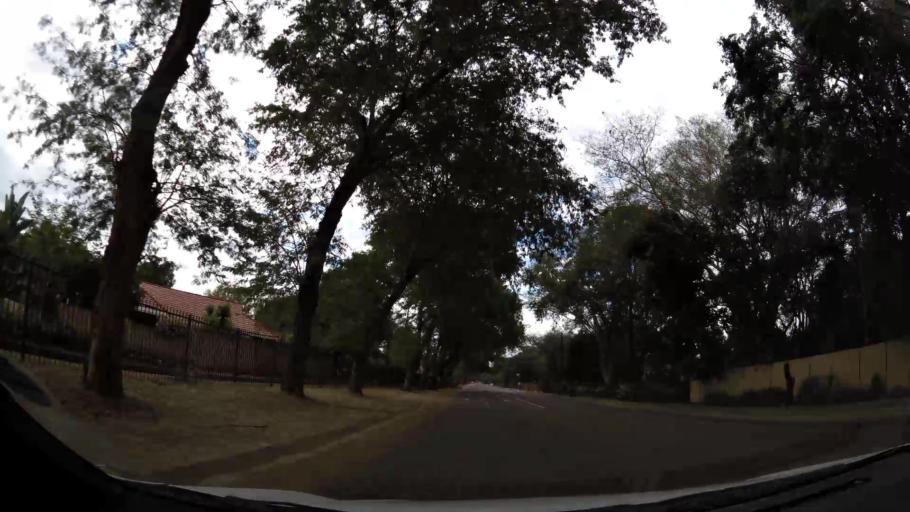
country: ZA
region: Limpopo
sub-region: Waterberg District Municipality
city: Modimolle
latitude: -24.5175
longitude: 28.7041
